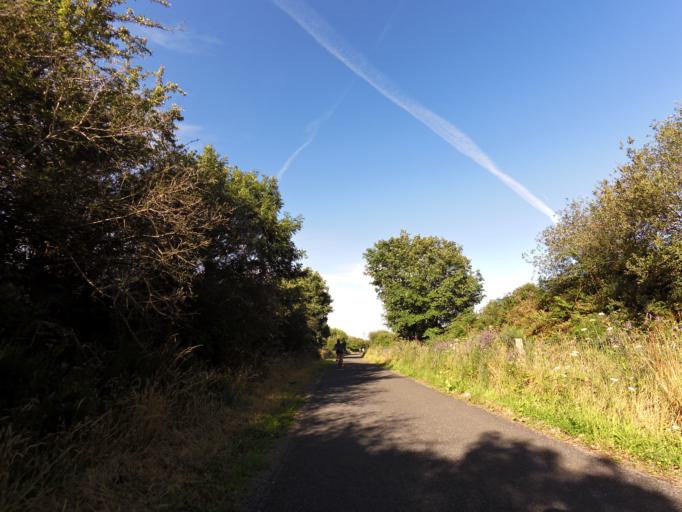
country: IE
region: Leinster
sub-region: Kilkenny
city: Mooncoin
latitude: 52.2448
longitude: -7.2608
